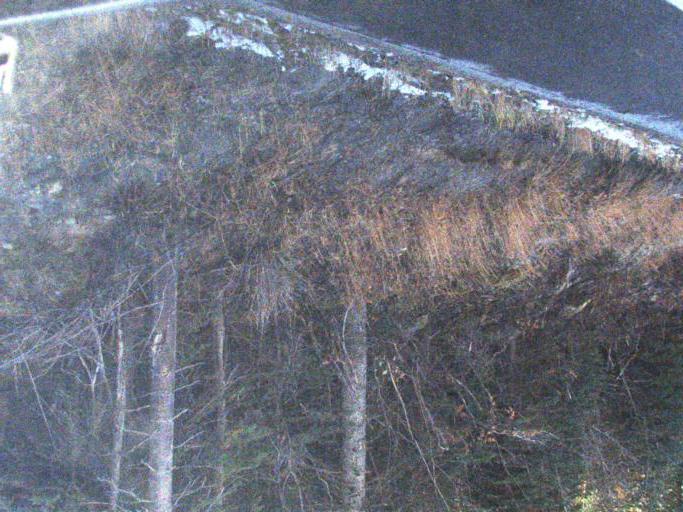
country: US
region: Washington
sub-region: Ferry County
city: Republic
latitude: 48.5952
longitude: -118.5143
